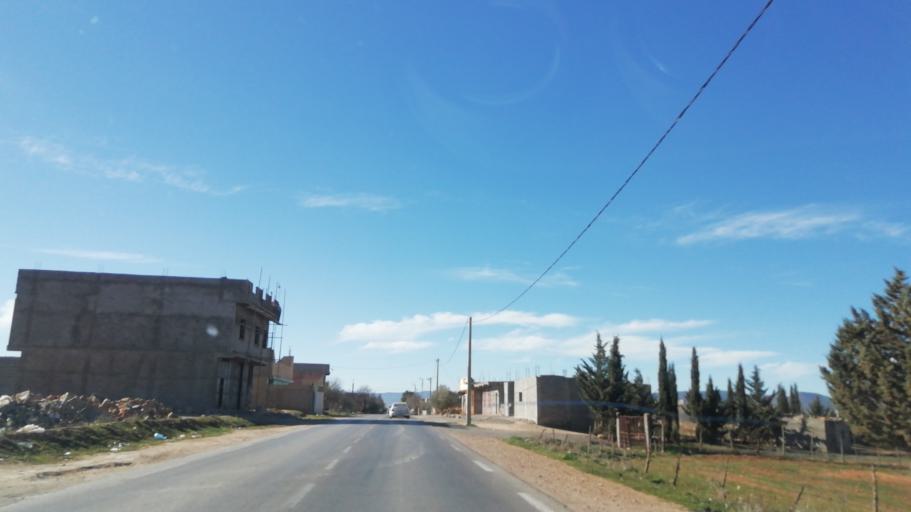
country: DZ
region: Tlemcen
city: Sebdou
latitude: 34.6760
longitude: -1.2664
